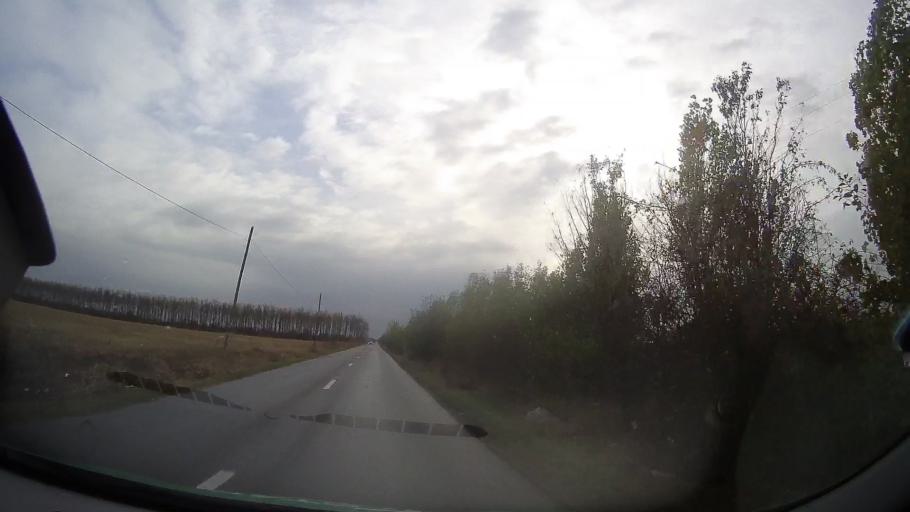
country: RO
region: Ialomita
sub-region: Comuna Fierbinti-Targ
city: Fierbintii de Jos
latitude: 44.7159
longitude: 26.3900
